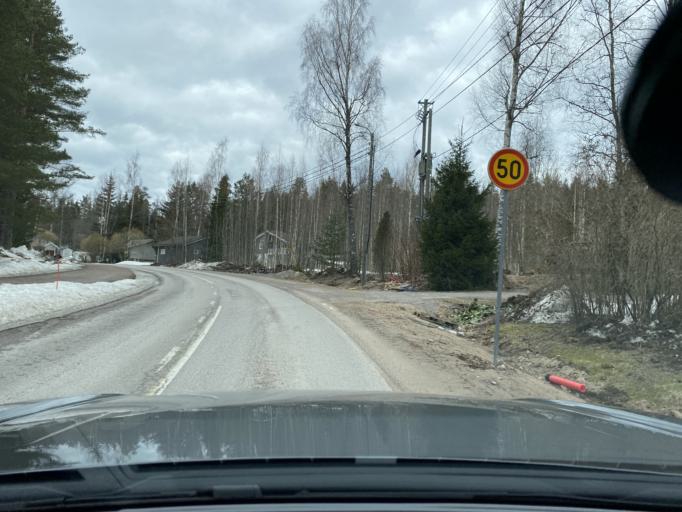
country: FI
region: Uusimaa
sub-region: Helsinki
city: Hyvinge
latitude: 60.5706
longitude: 24.7980
